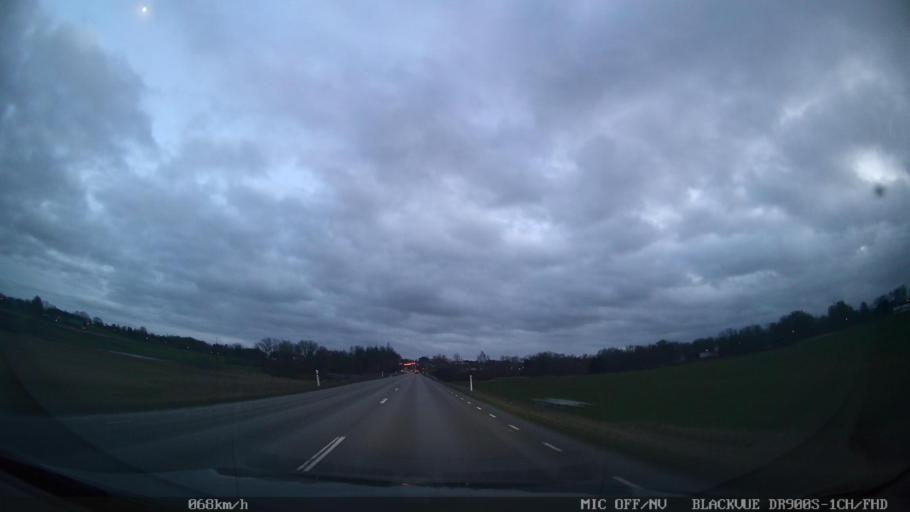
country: SE
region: Skane
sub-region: Hassleholms Kommun
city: Hassleholm
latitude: 56.1756
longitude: 13.7560
